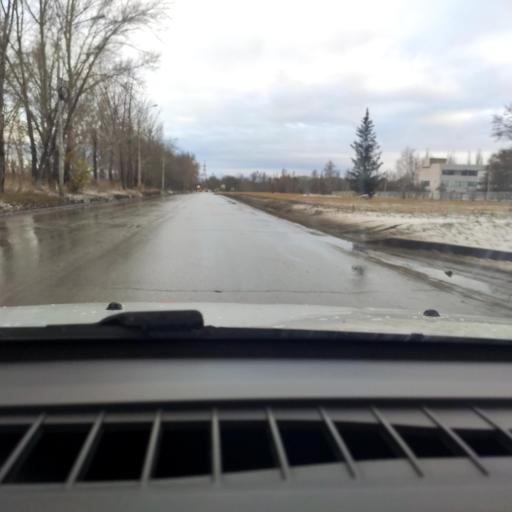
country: RU
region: Samara
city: Podstepki
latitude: 53.5819
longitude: 49.2207
